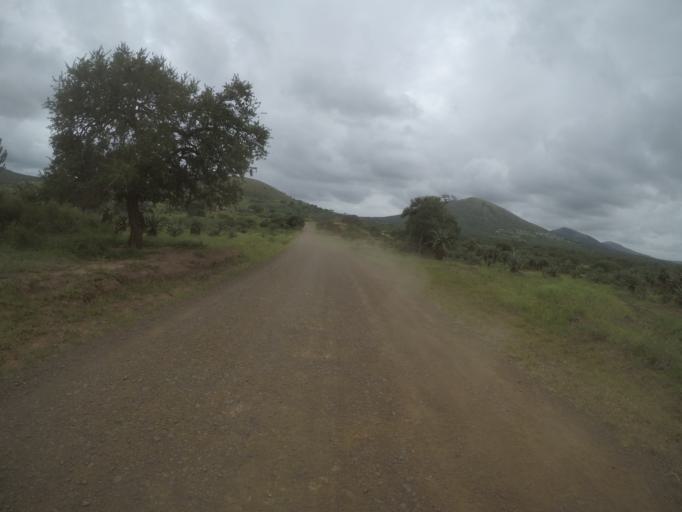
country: ZA
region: KwaZulu-Natal
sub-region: uThungulu District Municipality
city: Empangeni
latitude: -28.6053
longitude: 31.8703
